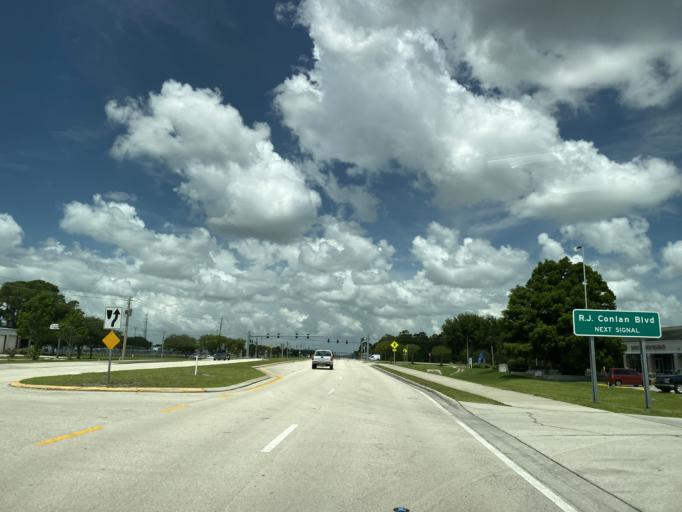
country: US
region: Florida
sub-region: Brevard County
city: Palm Bay
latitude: 28.0347
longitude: -80.5956
